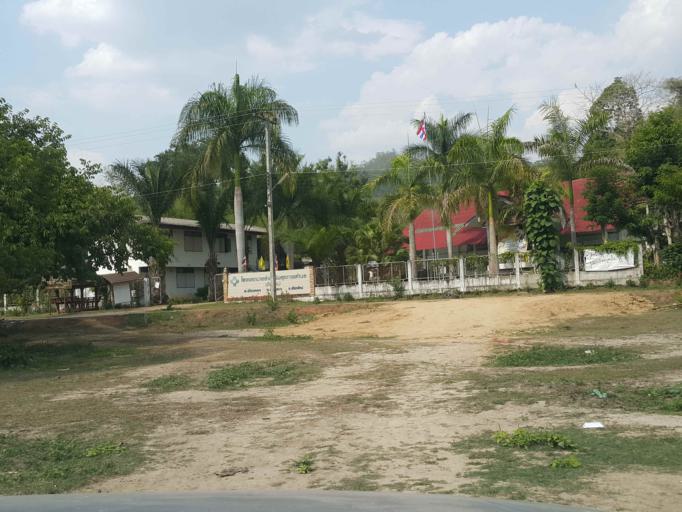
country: TH
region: Chiang Mai
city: Wiang Haeng
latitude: 19.3923
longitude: 98.7218
